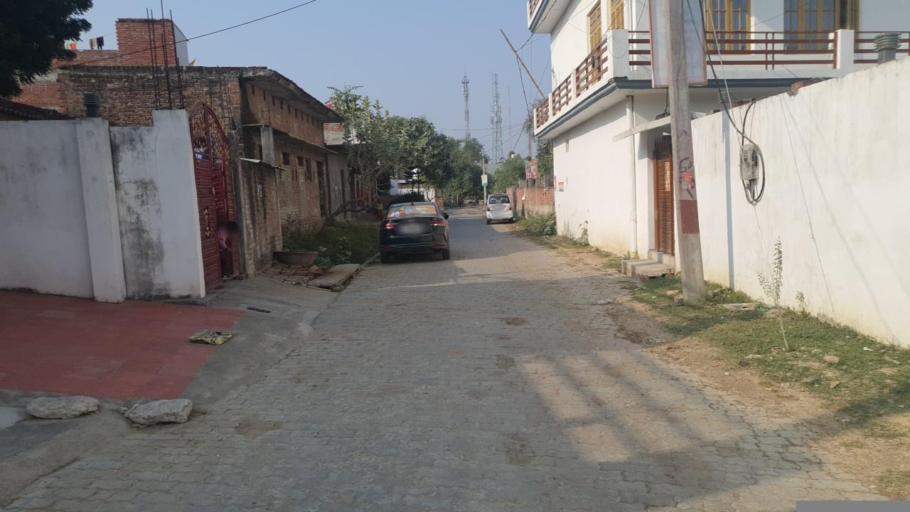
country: IN
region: Uttar Pradesh
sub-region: Lucknow District
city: Lucknow
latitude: 26.7956
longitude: 81.0095
